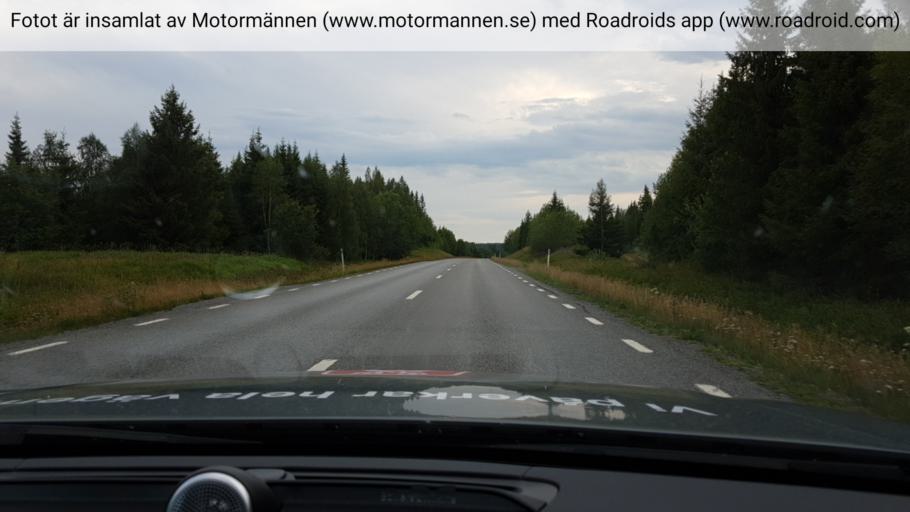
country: SE
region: Jaemtland
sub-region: OEstersunds Kommun
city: Lit
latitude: 63.4772
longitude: 15.2149
